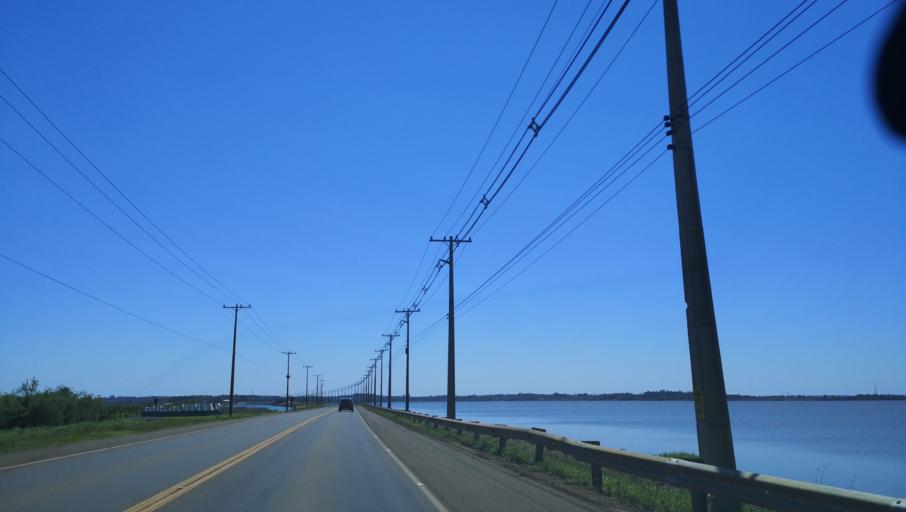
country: PY
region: Itapua
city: Carmen del Parana
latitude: -27.2098
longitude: -56.1594
